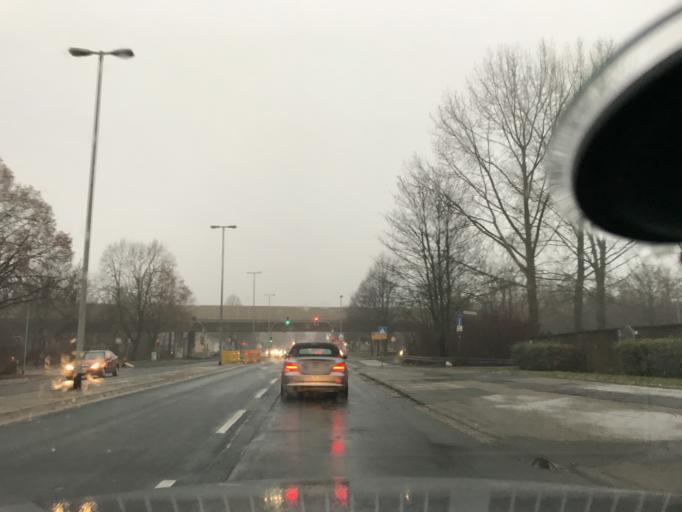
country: DE
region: Lower Saxony
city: Laatzen
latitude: 52.3535
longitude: 9.8273
